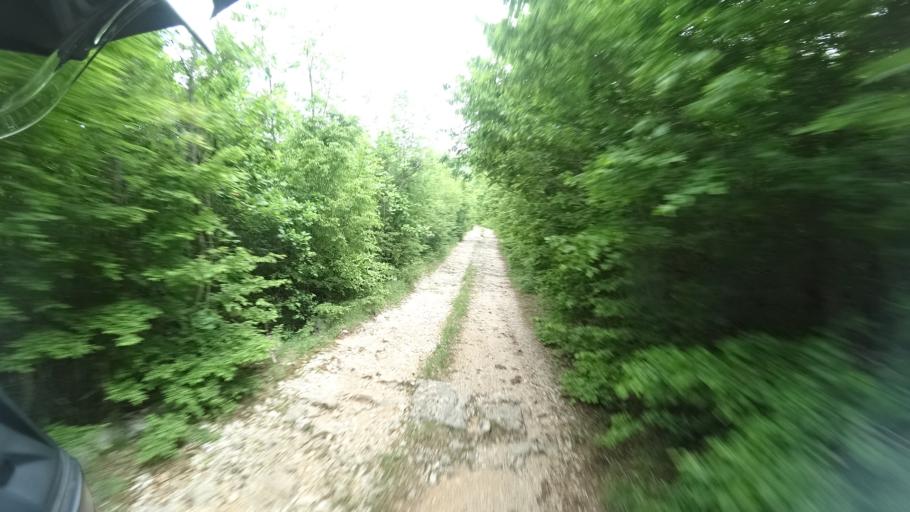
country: HR
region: Splitsko-Dalmatinska
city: Hrvace
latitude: 43.8928
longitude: 16.5404
